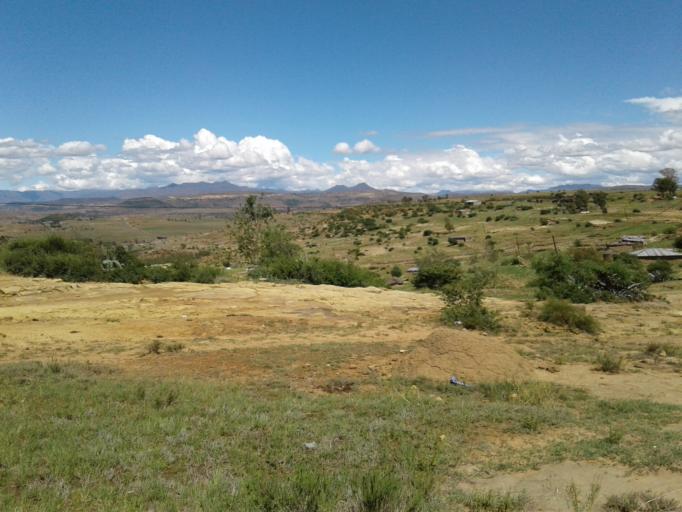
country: LS
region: Quthing
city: Quthing
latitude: -30.3653
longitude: 27.5479
